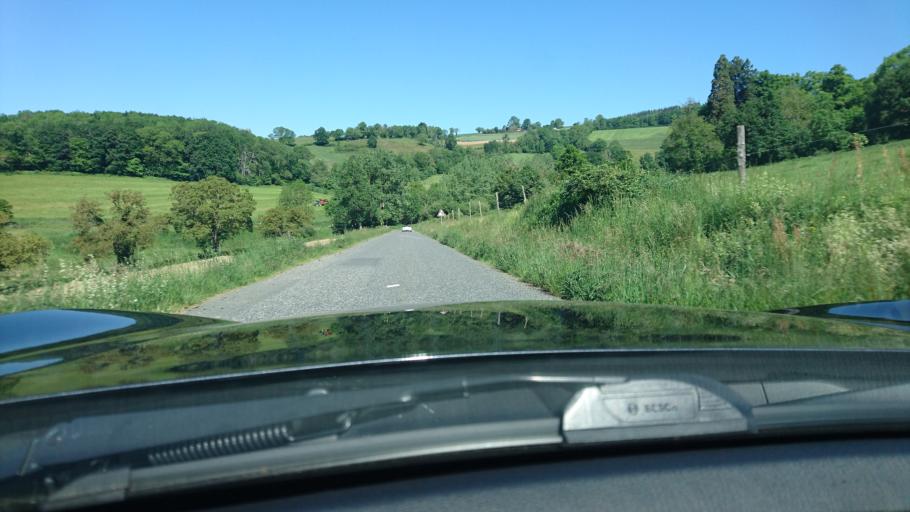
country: FR
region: Rhone-Alpes
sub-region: Departement de la Loire
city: Violay
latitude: 45.8289
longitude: 4.3851
